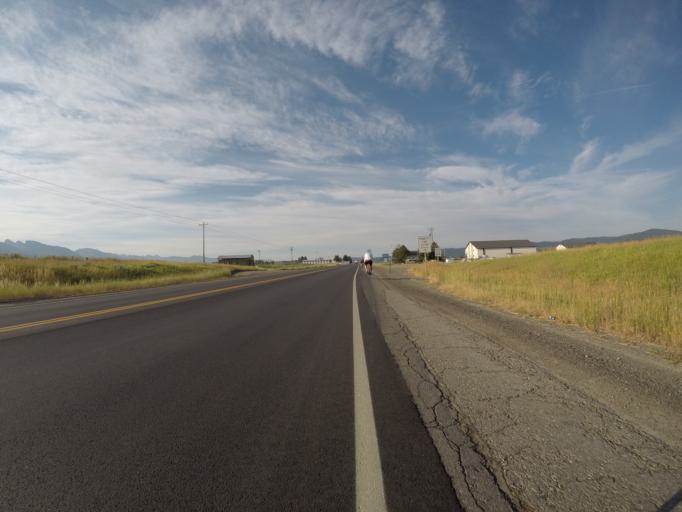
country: US
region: Wyoming
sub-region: Lincoln County
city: Afton
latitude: 42.9802
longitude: -111.0124
